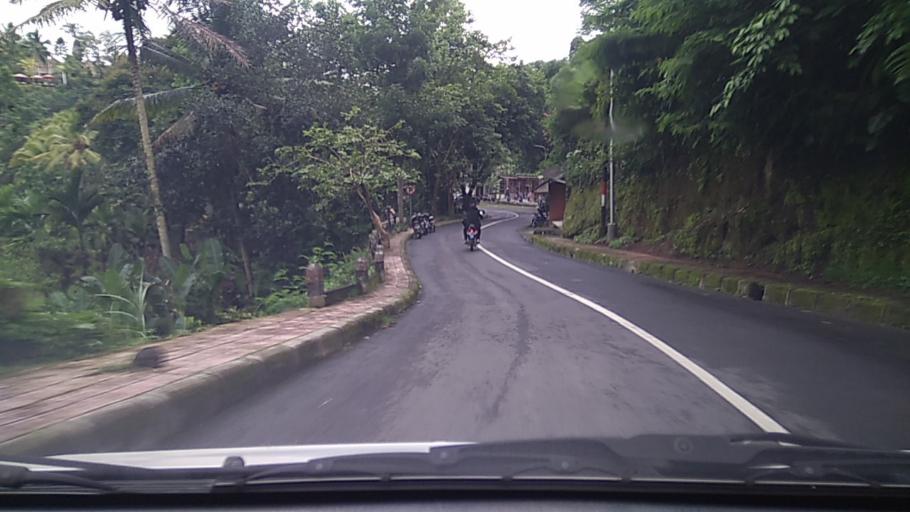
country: ID
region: Bali
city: Banjar Dujung Kaja
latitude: -8.4048
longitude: 115.2929
